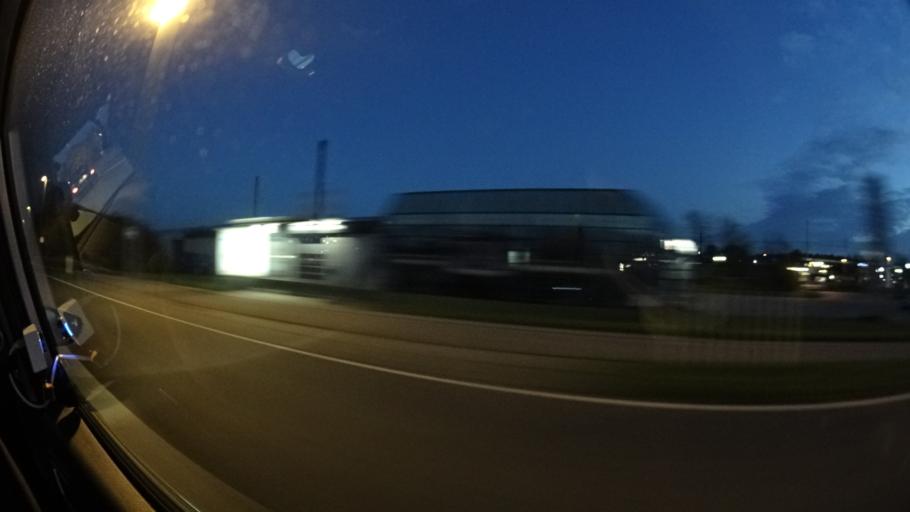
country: DK
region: South Denmark
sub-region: Odense Kommune
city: Hojby
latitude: 55.3449
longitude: 10.4443
